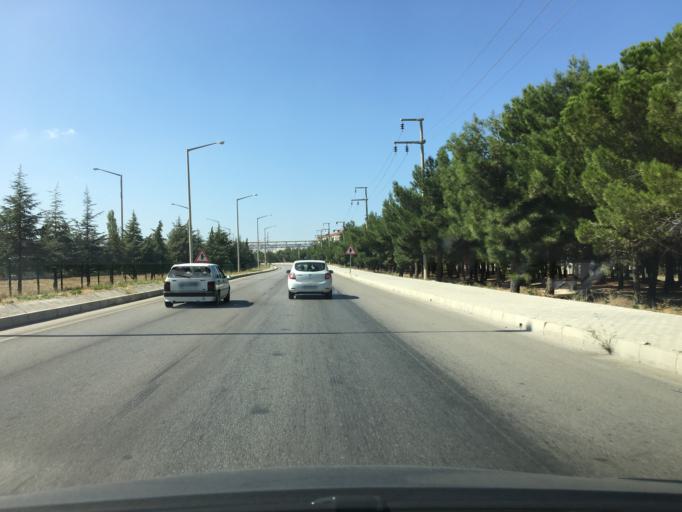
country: TR
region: Burdur
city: Burdur
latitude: 37.7292
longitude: 30.3040
